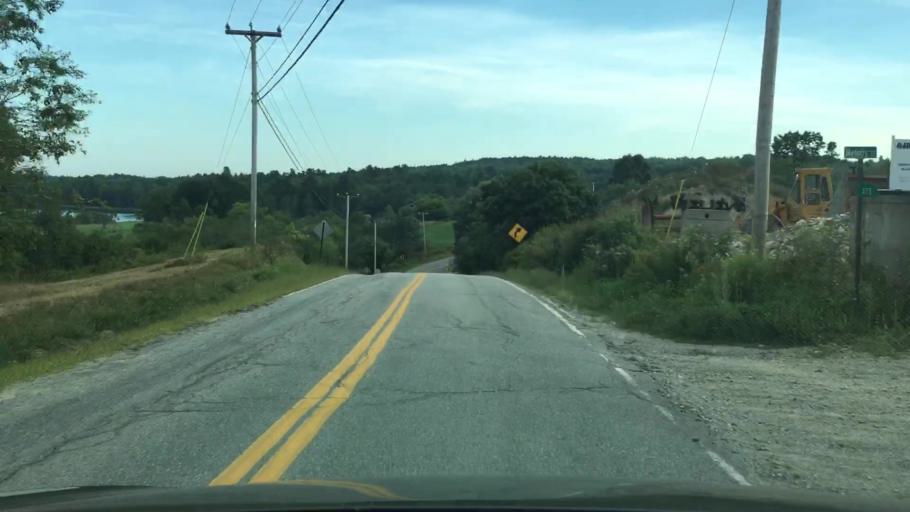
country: US
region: Maine
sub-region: Hancock County
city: Penobscot
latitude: 44.4707
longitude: -68.7386
